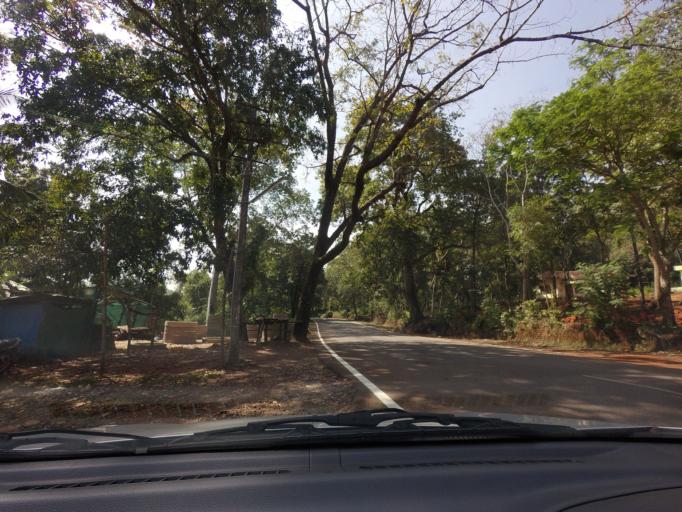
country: IN
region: Karnataka
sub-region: Dakshina Kannada
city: Sulya
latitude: 12.6794
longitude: 75.6101
